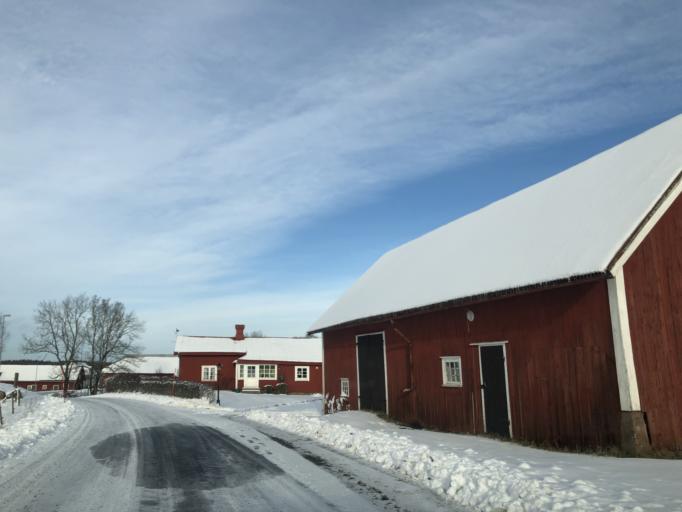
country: SE
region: Vaestra Goetaland
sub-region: Ulricehamns Kommun
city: Ulricehamn
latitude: 57.7812
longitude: 13.5243
